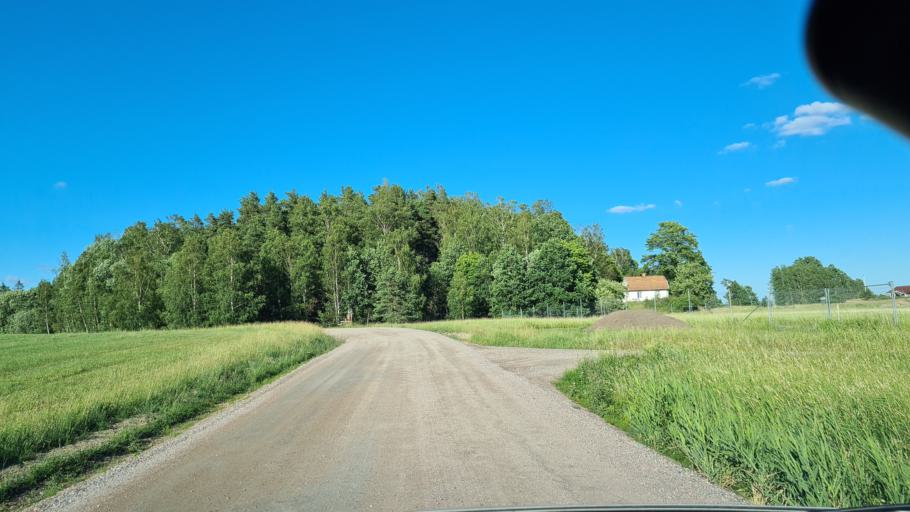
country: SE
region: Soedermanland
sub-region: Nykopings Kommun
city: Nykoping
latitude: 58.9156
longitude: 17.0022
